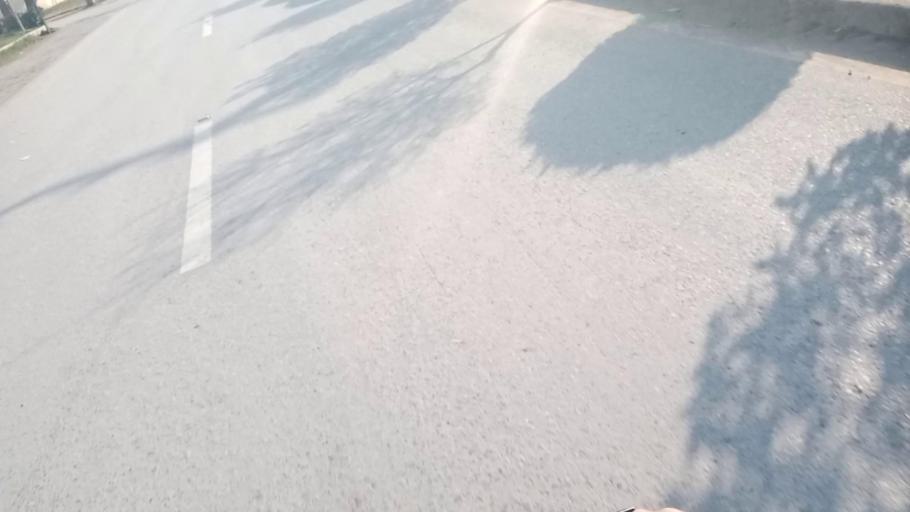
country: PK
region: Khyber Pakhtunkhwa
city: Peshawar
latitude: 33.9909
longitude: 71.4458
